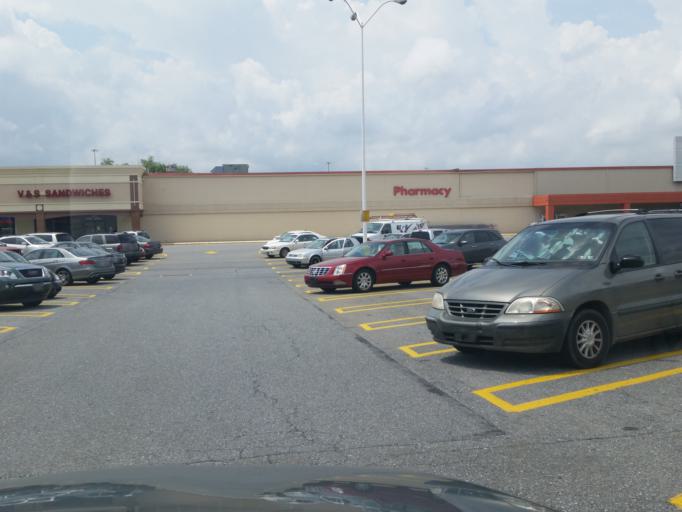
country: US
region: Pennsylvania
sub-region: Lancaster County
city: Lancaster
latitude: 40.0727
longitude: -76.3204
